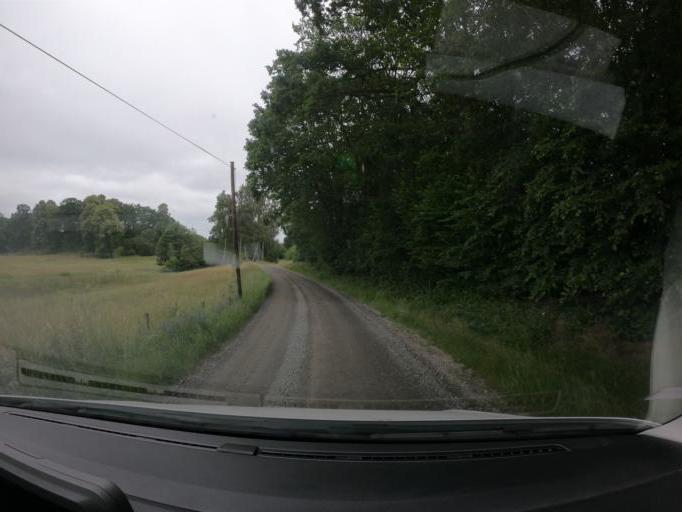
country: SE
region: Skane
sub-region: Hoors Kommun
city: Hoeoer
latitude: 56.0053
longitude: 13.4781
